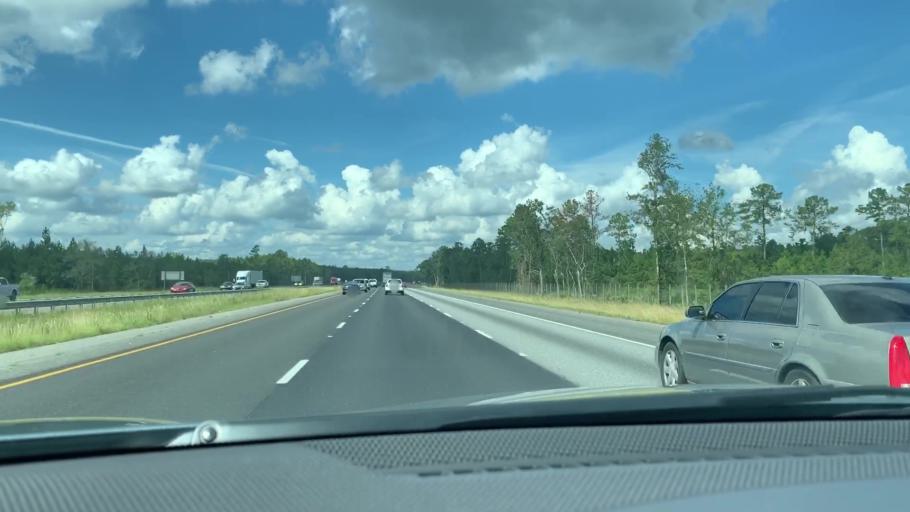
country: US
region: Georgia
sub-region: Camden County
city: Kingsland
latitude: 30.8644
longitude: -81.6805
